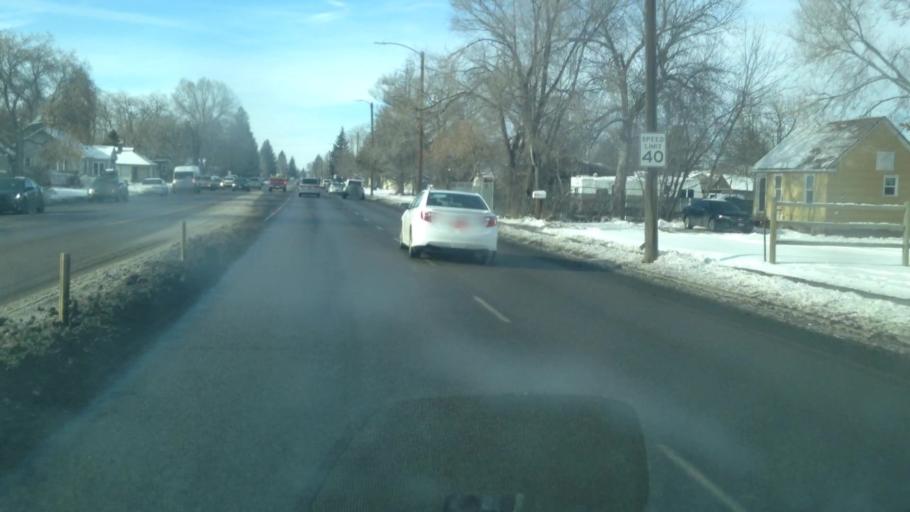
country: US
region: Idaho
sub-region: Bonneville County
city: Idaho Falls
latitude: 43.4826
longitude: -112.0245
